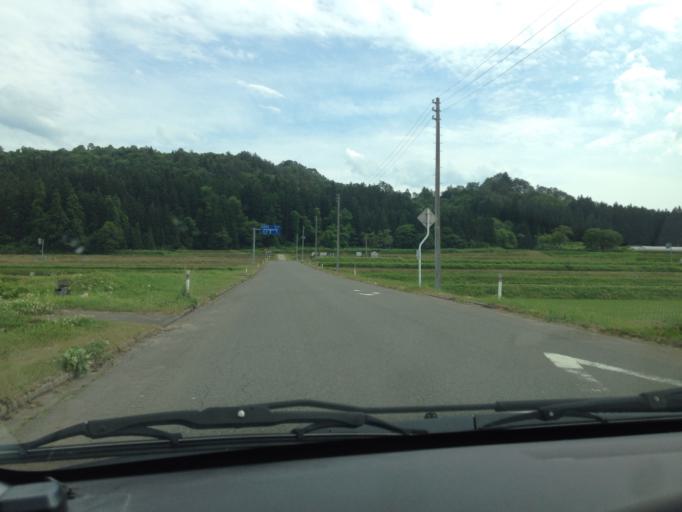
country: JP
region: Fukushima
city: Kitakata
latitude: 37.5035
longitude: 139.7179
